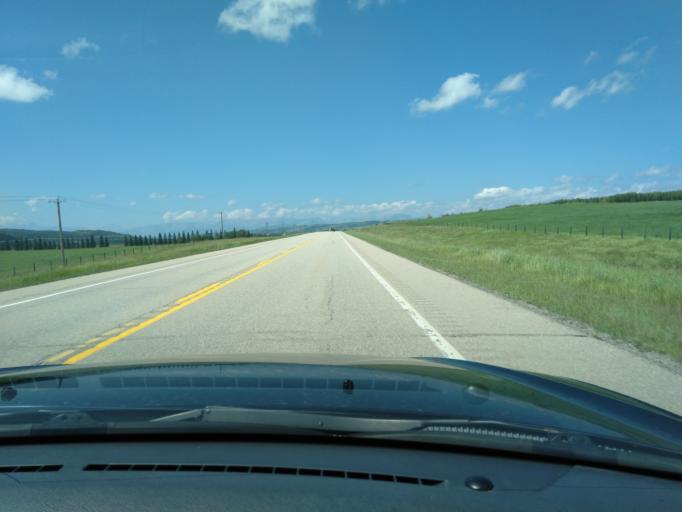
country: CA
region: Alberta
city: Cochrane
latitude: 51.2245
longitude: -114.6614
